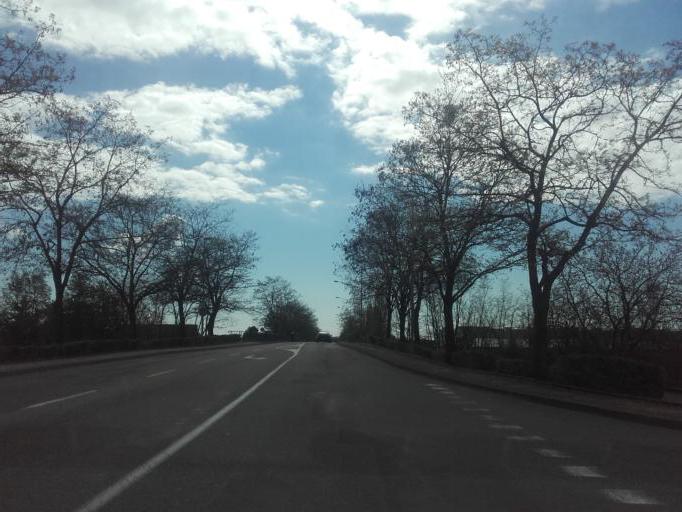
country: FR
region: Bourgogne
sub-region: Departement de la Cote-d'Or
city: Nuits-Saint-Georges
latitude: 47.1350
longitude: 4.9578
